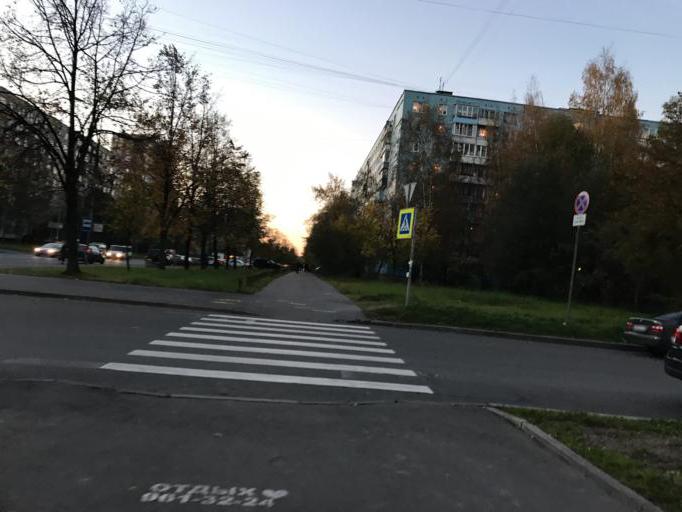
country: RU
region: St.-Petersburg
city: Obukhovo
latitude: 59.8992
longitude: 30.4734
